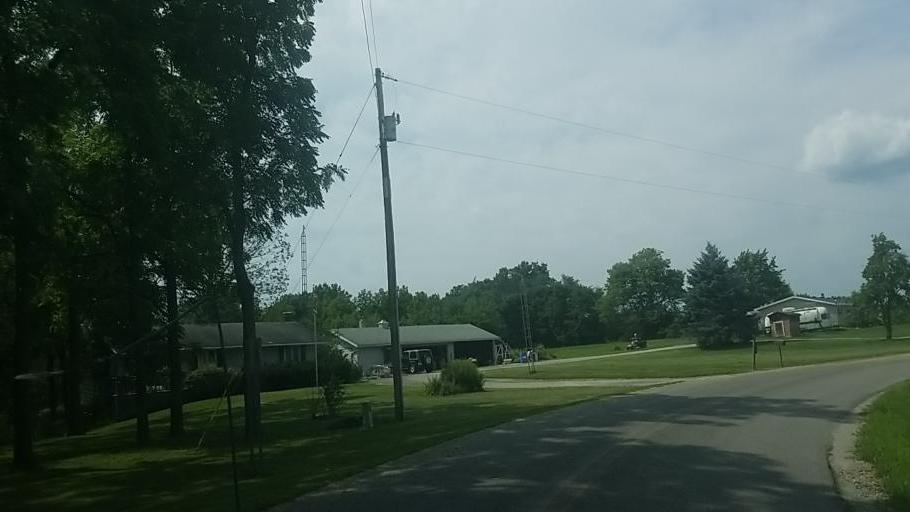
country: US
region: Ohio
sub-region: Hardin County
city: Forest
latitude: 40.8014
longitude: -83.5524
